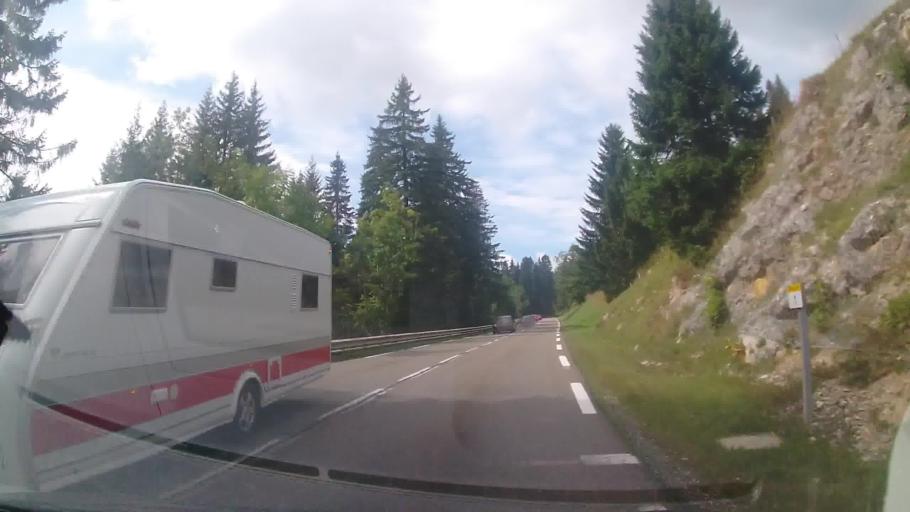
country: FR
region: Franche-Comte
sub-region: Departement du Jura
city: Les Rousses
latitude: 46.4108
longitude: 6.0647
